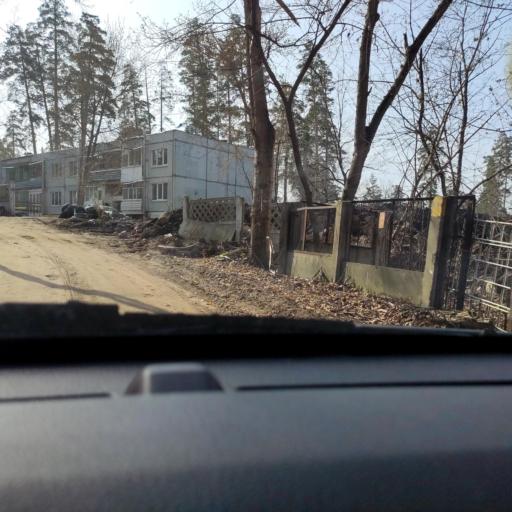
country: RU
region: Samara
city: Tol'yatti
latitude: 53.4905
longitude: 49.3027
